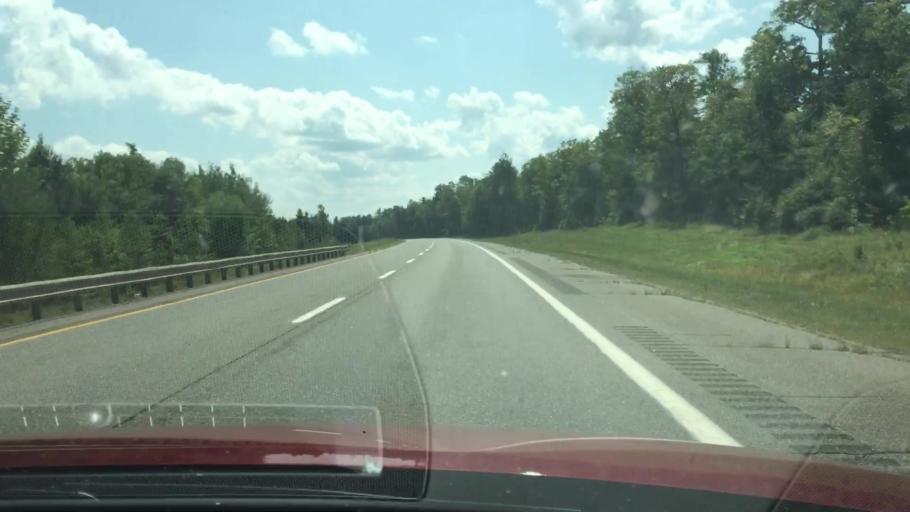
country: US
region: Maine
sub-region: Penobscot County
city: Lincoln
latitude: 45.4568
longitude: -68.5909
